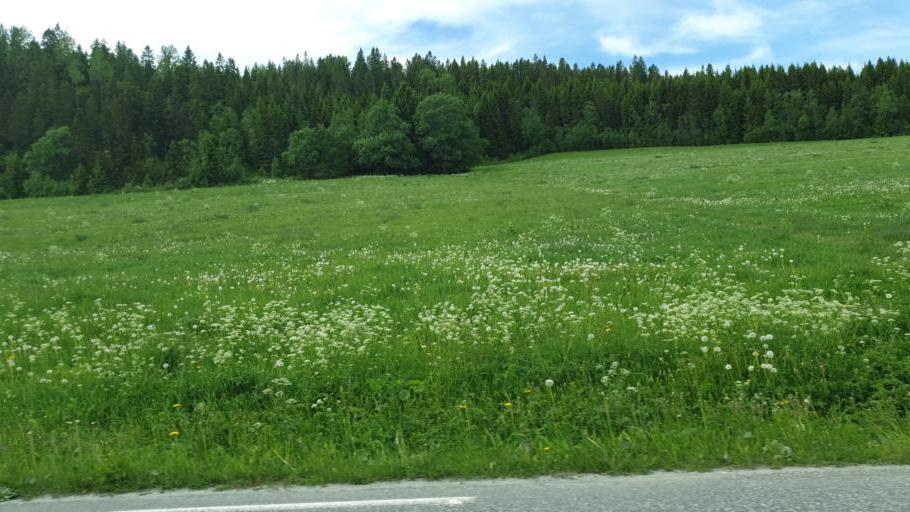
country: NO
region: Nord-Trondelag
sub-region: Leksvik
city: Leksvik
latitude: 63.6579
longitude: 10.6085
